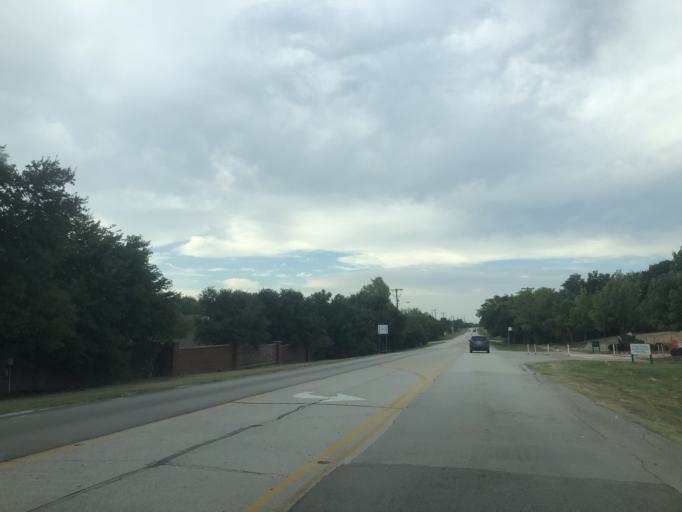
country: US
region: Texas
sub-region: Tarrant County
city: Southlake
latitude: 32.9511
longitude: -97.1511
